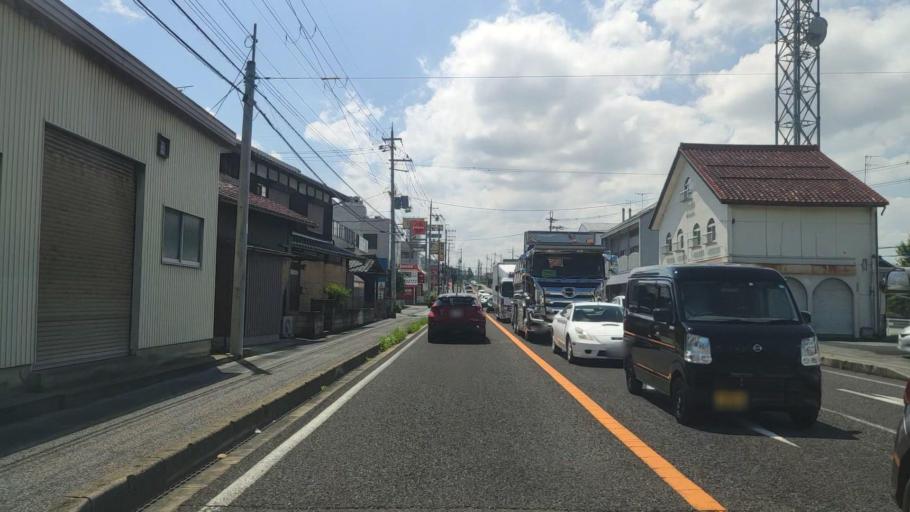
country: JP
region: Shiga Prefecture
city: Hikone
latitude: 35.2661
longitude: 136.2680
